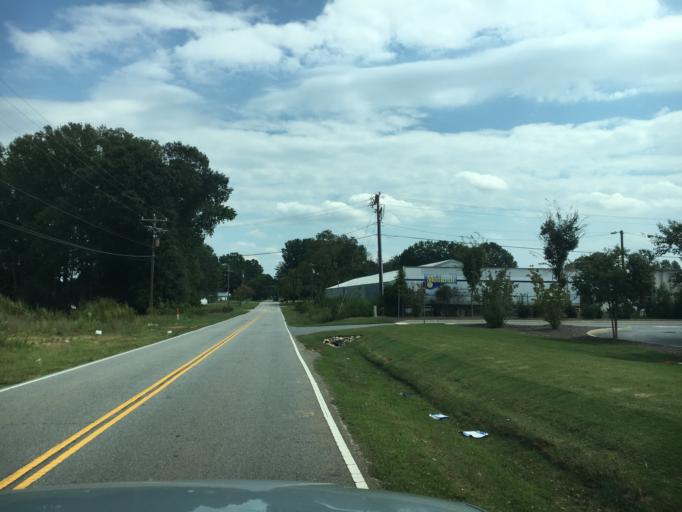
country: US
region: South Carolina
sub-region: Anderson County
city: Powdersville
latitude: 34.7874
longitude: -82.4777
